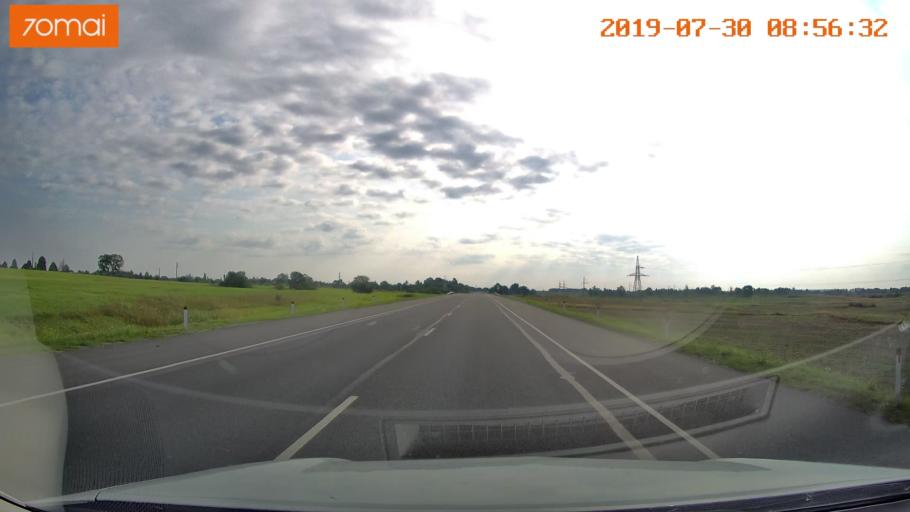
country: RU
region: Kaliningrad
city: Gusev
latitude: 54.6002
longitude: 22.0794
